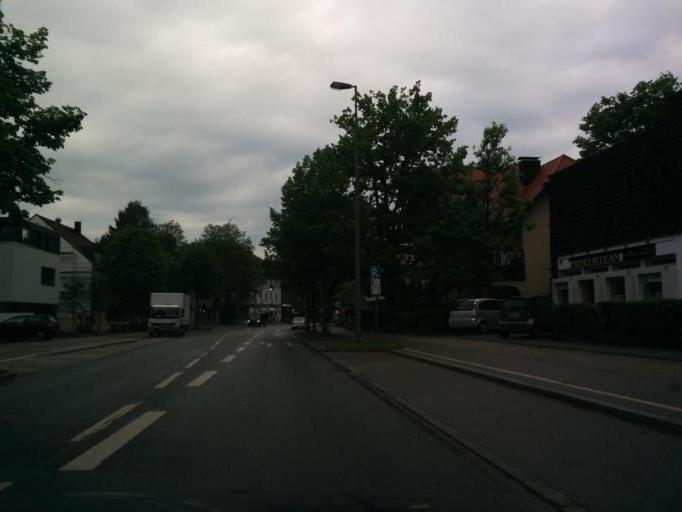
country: DE
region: Bavaria
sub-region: Upper Bavaria
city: Pullach im Isartal
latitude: 48.0802
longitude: 11.5282
